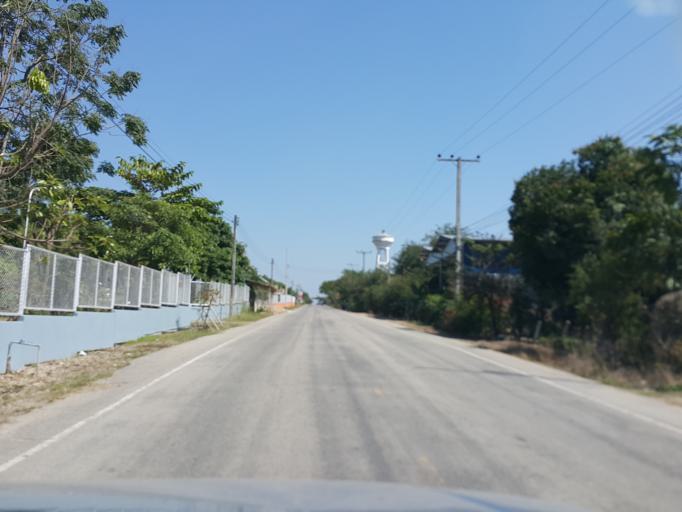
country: TH
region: Chiang Mai
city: Doi Lo
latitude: 18.5335
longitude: 98.7915
